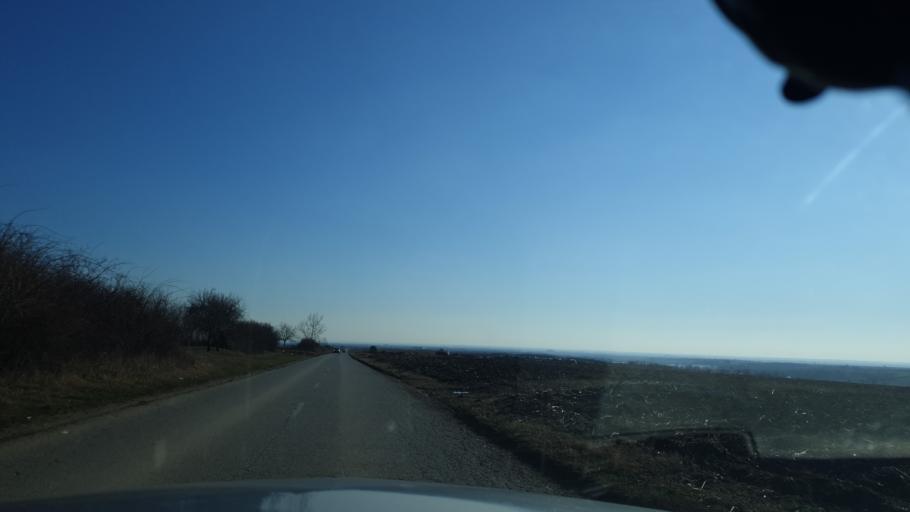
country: RS
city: Vrdnik
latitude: 45.0910
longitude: 19.8060
